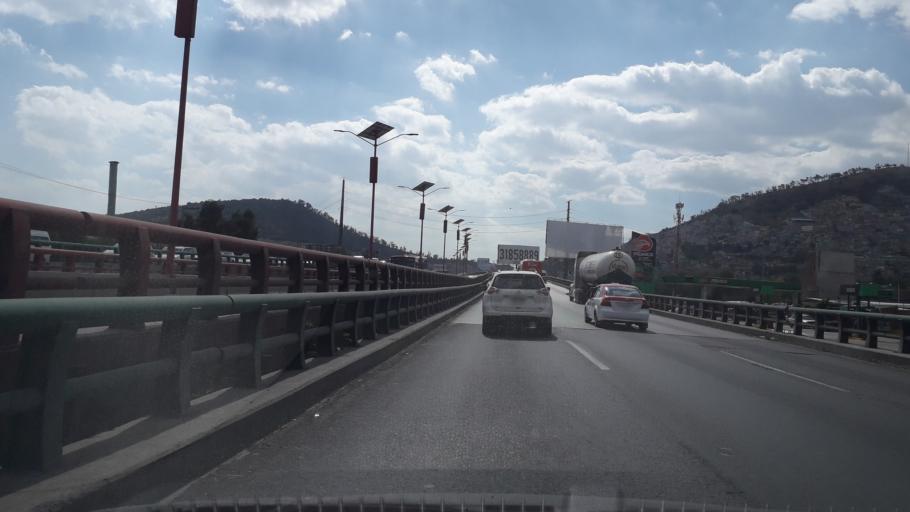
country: MX
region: Mexico City
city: Gustavo A. Madero
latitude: 19.5168
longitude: -99.1003
